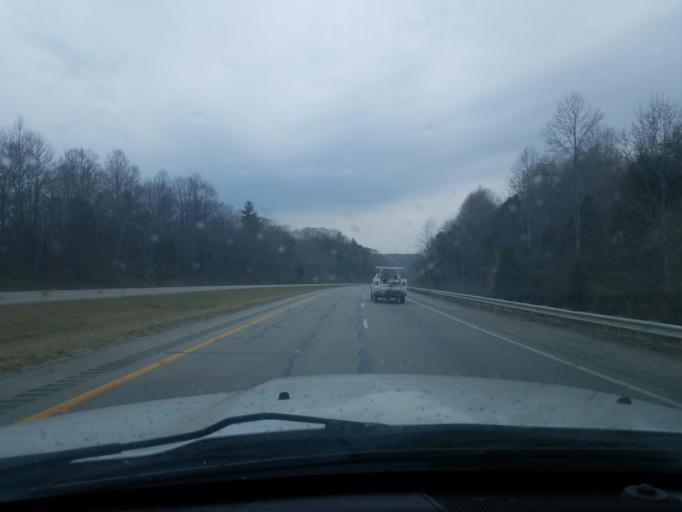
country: US
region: Kentucky
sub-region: Rowan County
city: Morehead
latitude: 38.1896
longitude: -83.4850
